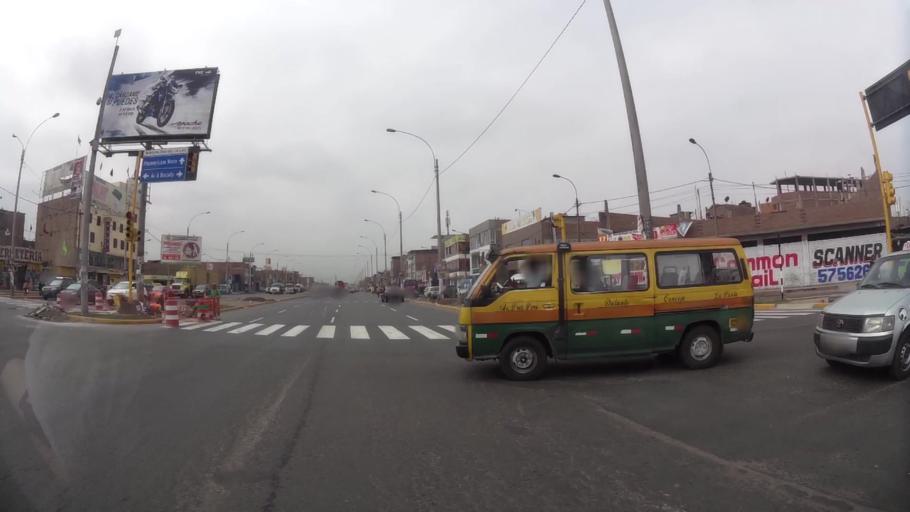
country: PE
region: Callao
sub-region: Callao
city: Callao
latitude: -11.9969
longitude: -77.1126
